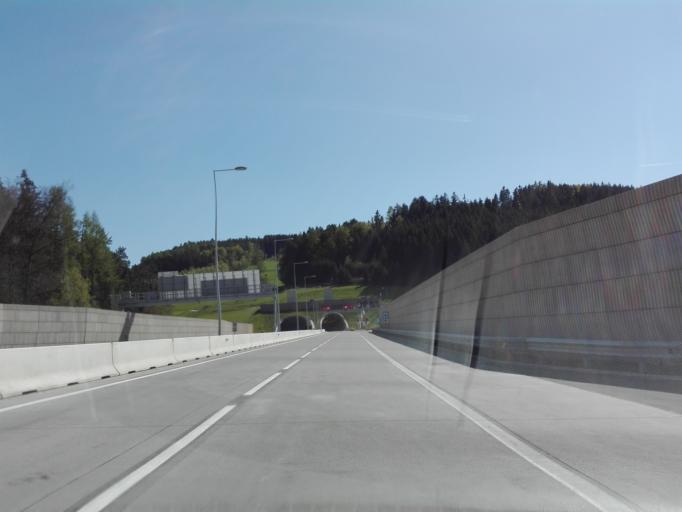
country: AT
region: Upper Austria
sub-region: Politischer Bezirk Urfahr-Umgebung
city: Alberndorf in der Riedmark
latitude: 48.4116
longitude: 14.4843
